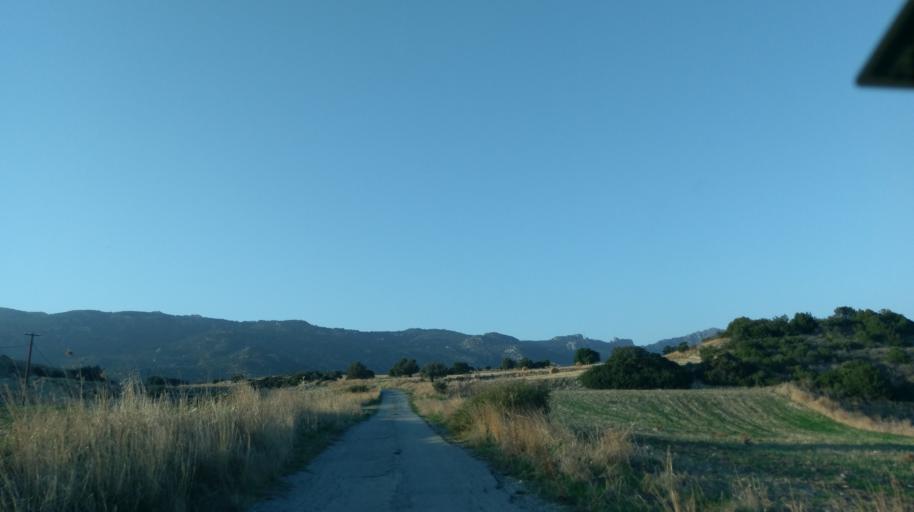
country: CY
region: Ammochostos
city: Trikomo
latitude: 35.3639
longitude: 33.9142
